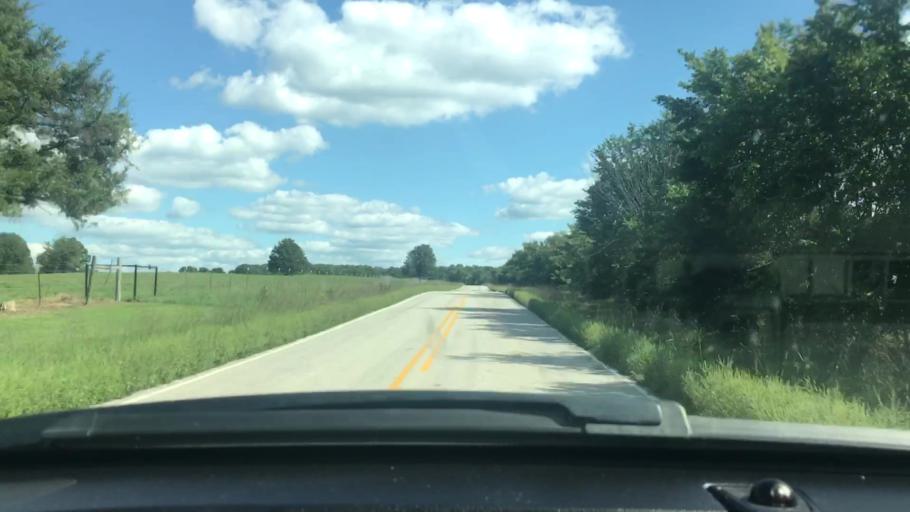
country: US
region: Missouri
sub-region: Wright County
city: Hartville
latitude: 37.3807
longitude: -92.4371
